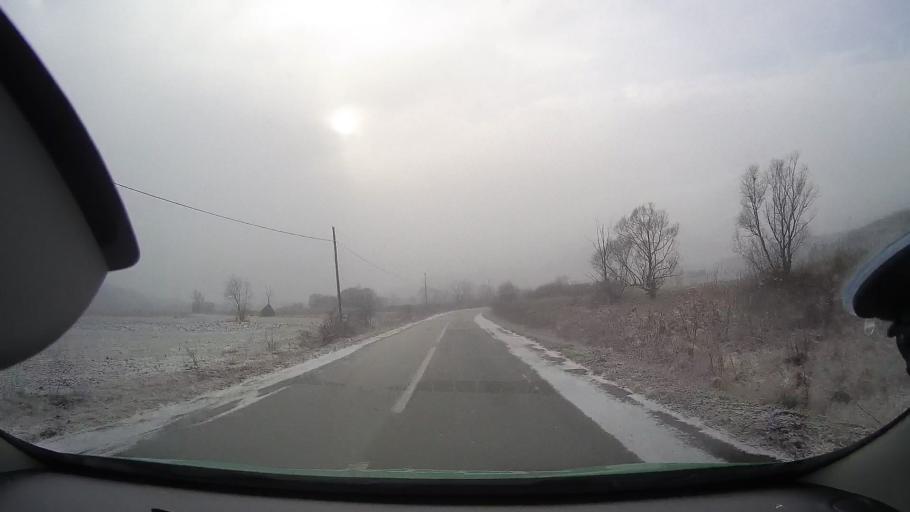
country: RO
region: Alba
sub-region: Comuna Rimetea
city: Rimetea
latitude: 46.4071
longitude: 23.5577
